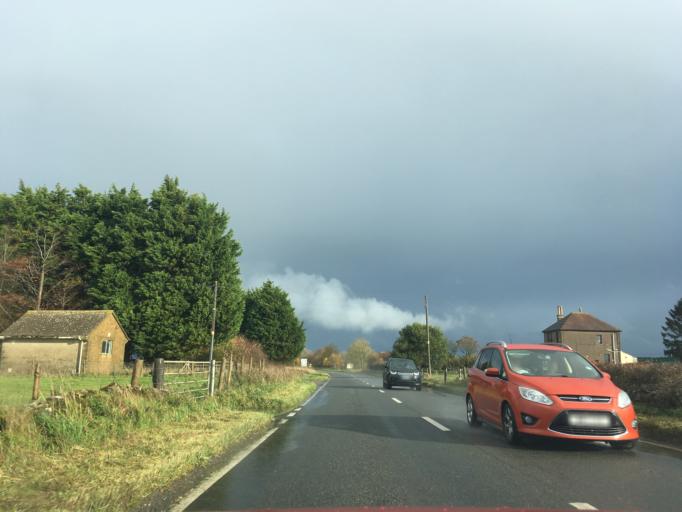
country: GB
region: England
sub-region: South Gloucestershire
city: Marshfield
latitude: 51.4611
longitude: -2.3361
